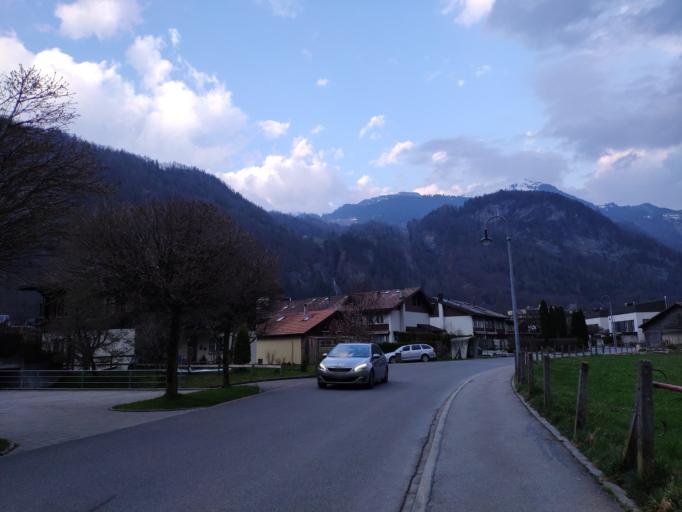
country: CH
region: Bern
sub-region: Interlaken-Oberhasli District
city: Meiringen
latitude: 46.7262
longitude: 8.1832
